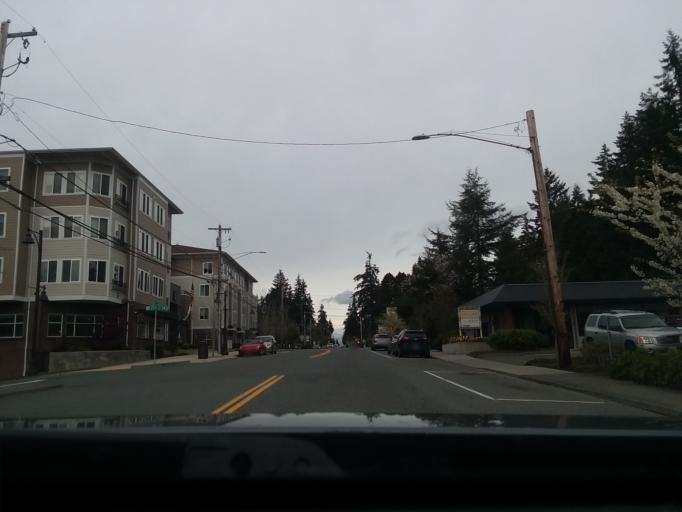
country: US
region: Washington
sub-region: Snohomish County
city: Mountlake Terrace
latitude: 47.7892
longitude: -122.3085
